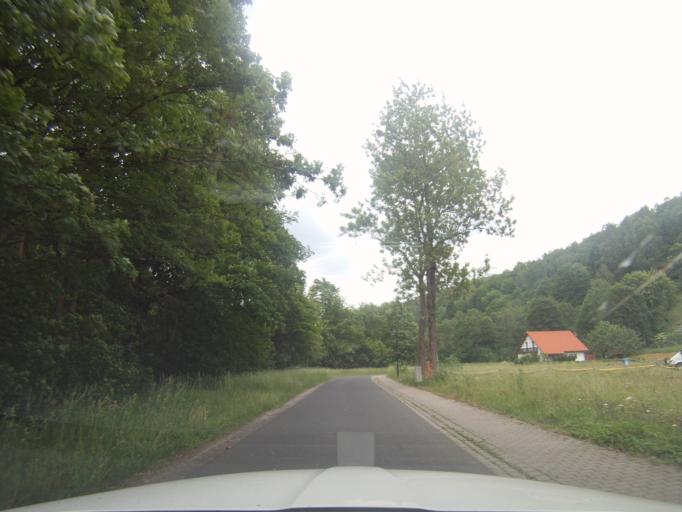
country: DE
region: Thuringia
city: Frauenwald
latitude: 50.5262
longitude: 10.8795
